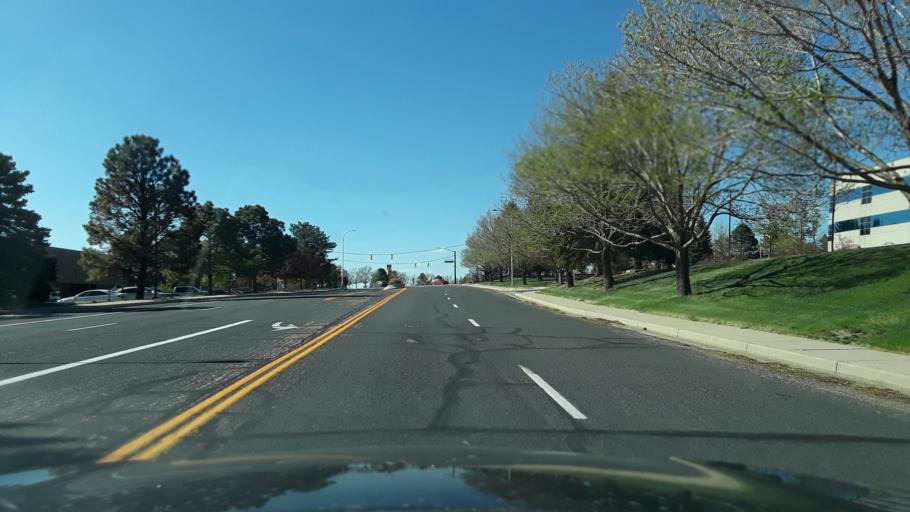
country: US
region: Colorado
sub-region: El Paso County
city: Air Force Academy
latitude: 38.9582
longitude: -104.7908
